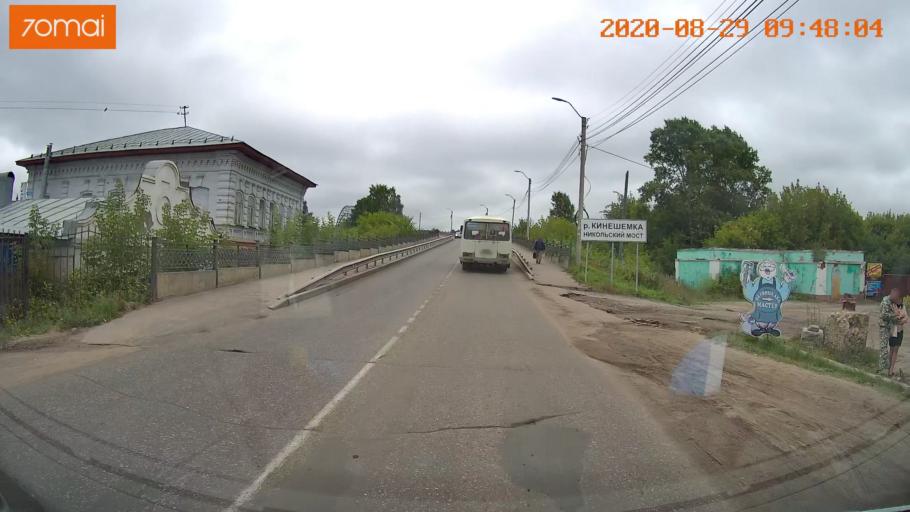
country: RU
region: Ivanovo
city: Kineshma
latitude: 57.4415
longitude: 42.1716
